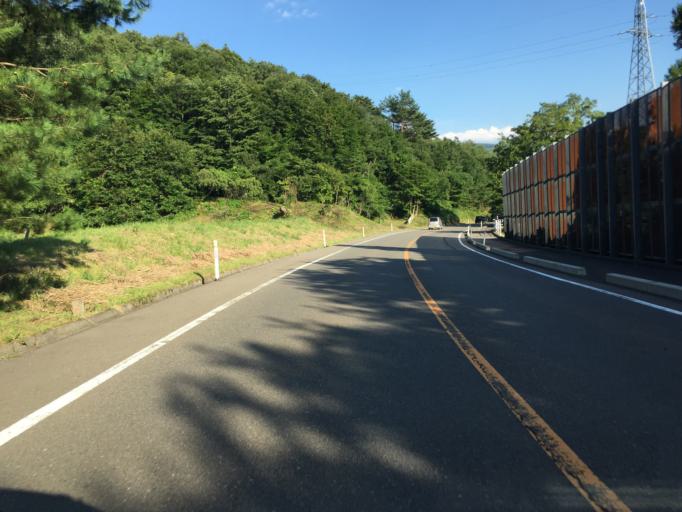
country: JP
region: Miyagi
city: Shiroishi
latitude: 37.9588
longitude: 140.5289
